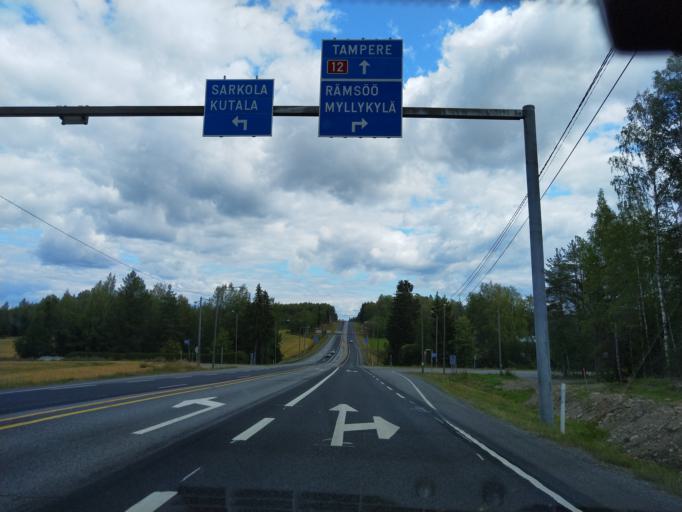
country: FI
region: Pirkanmaa
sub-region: Tampere
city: Haemeenkyroe
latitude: 61.3988
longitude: 23.2526
